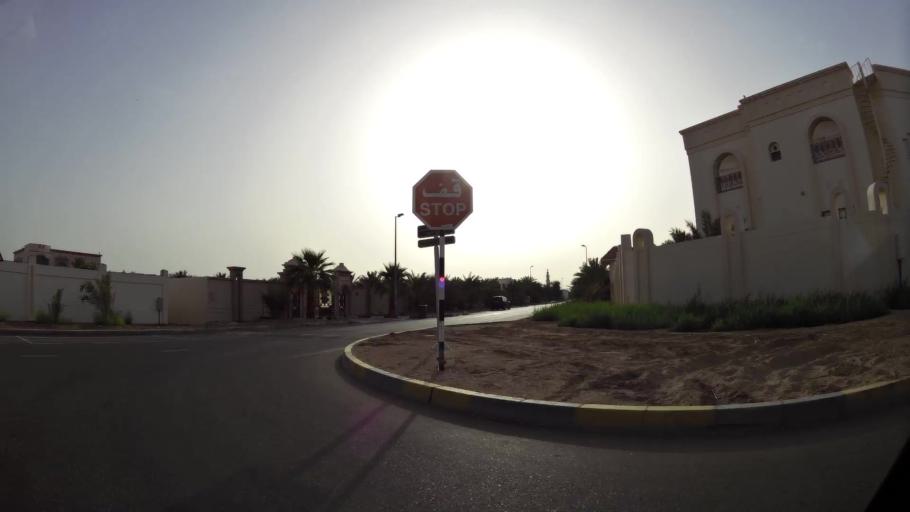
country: AE
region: Abu Dhabi
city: Al Ain
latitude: 24.1241
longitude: 55.7087
